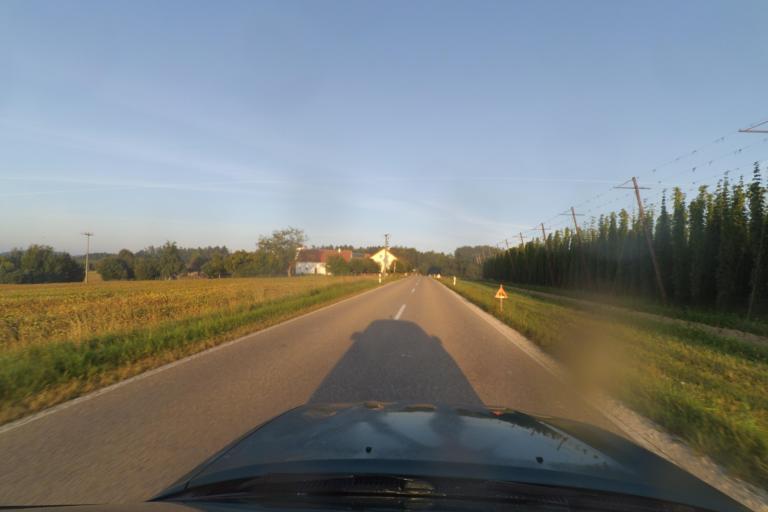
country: DE
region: Bavaria
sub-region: Lower Bavaria
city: Mainburg
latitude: 48.6540
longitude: 11.7539
